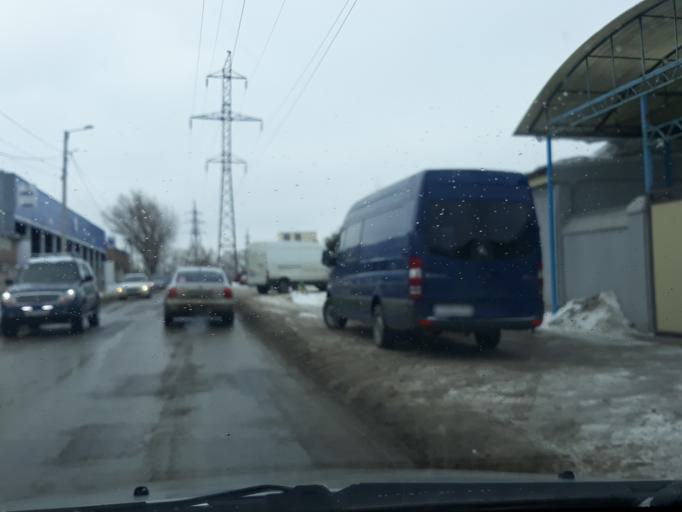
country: RU
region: Rostov
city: Taganrog
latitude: 47.2473
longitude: 38.8904
